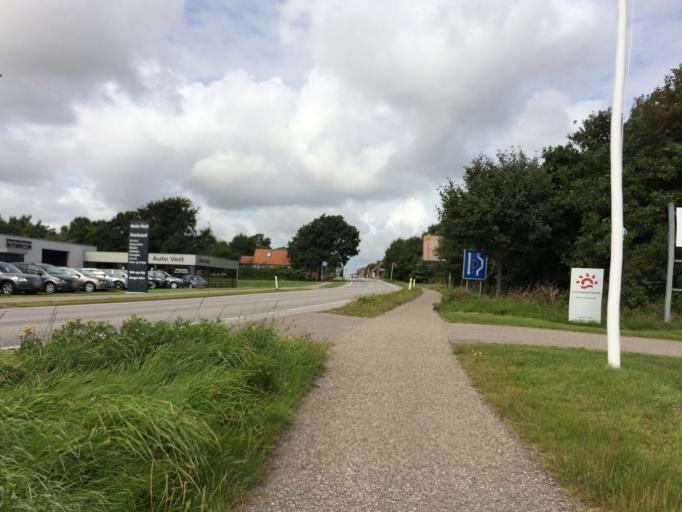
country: DK
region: Central Jutland
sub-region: Holstebro Kommune
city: Ulfborg
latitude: 56.3388
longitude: 8.3459
